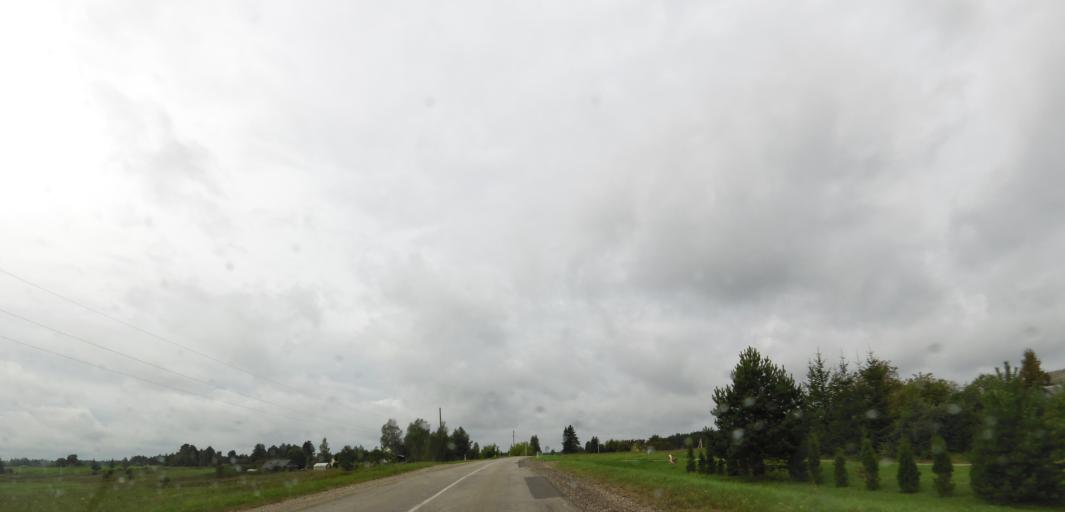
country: LT
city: Moletai
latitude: 55.2113
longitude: 25.3189
